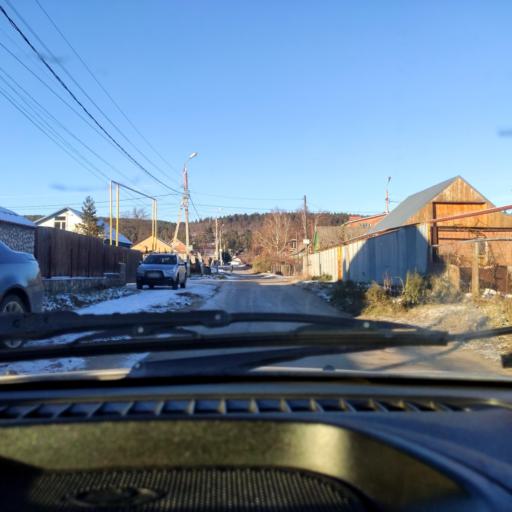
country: RU
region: Samara
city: Zhigulevsk
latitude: 53.4666
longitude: 49.6035
